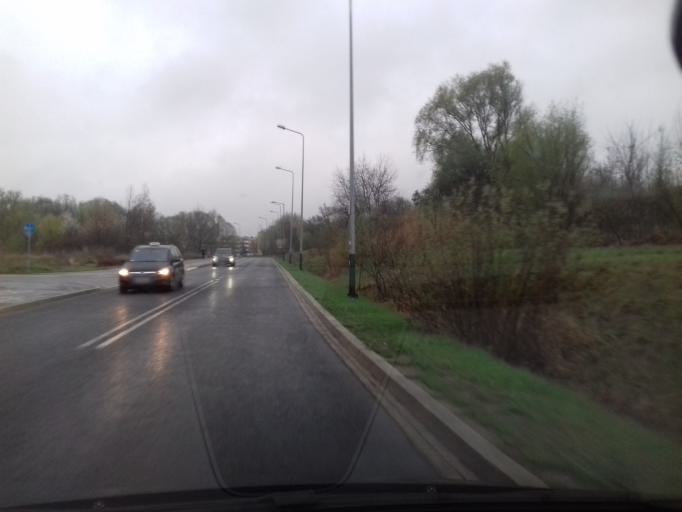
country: PL
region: Lesser Poland Voivodeship
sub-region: Krakow
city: Krakow
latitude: 50.0251
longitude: 19.9529
